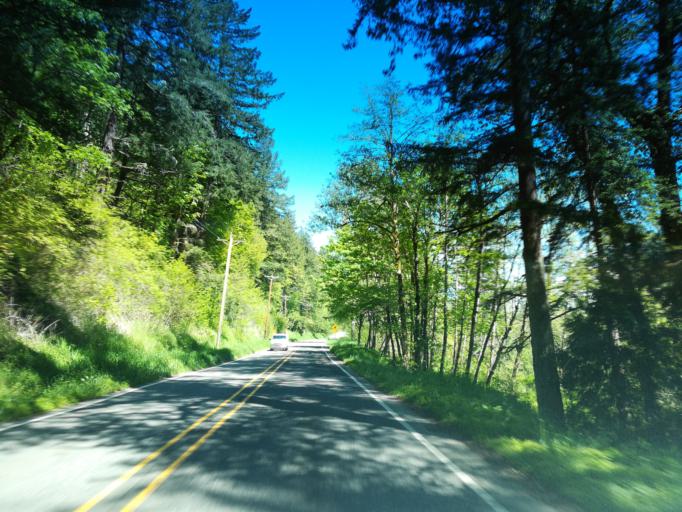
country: US
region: Oregon
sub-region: Multnomah County
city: Troutdale
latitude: 45.5182
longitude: -122.3526
